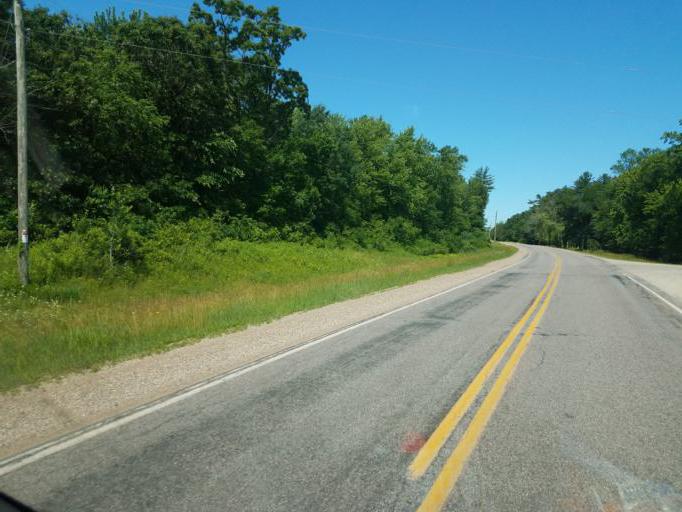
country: US
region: Wisconsin
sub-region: Adams County
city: Adams
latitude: 43.8133
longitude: -89.8915
